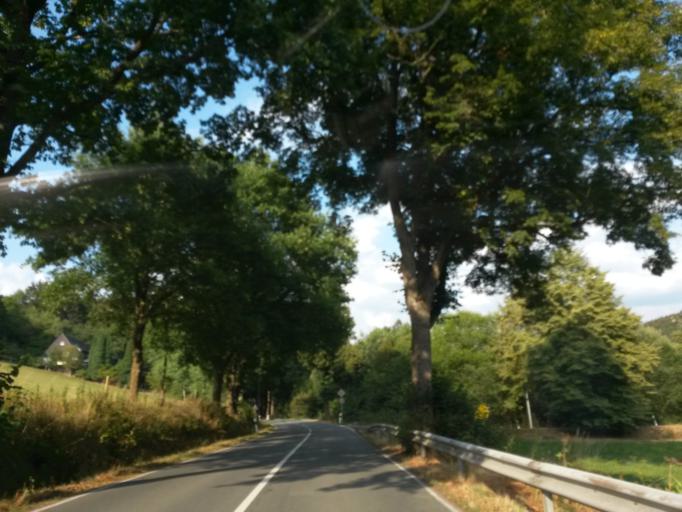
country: DE
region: North Rhine-Westphalia
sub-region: Regierungsbezirk Koln
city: Marienheide
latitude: 51.0526
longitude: 7.4963
